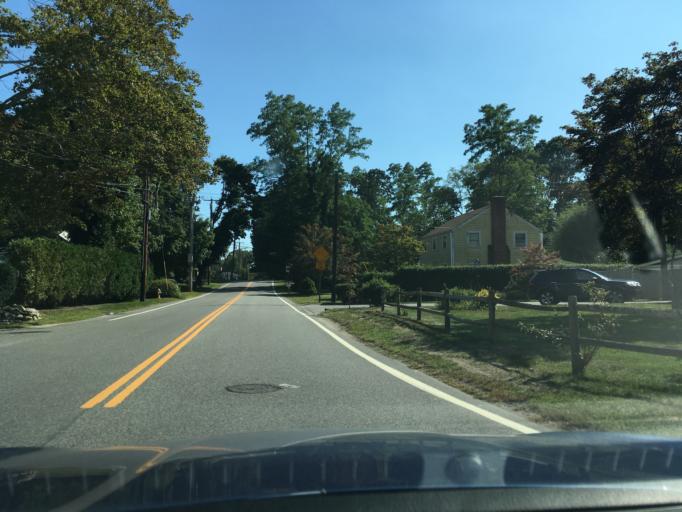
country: US
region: Rhode Island
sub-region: Bristol County
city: Barrington
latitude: 41.7390
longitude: -71.3304
